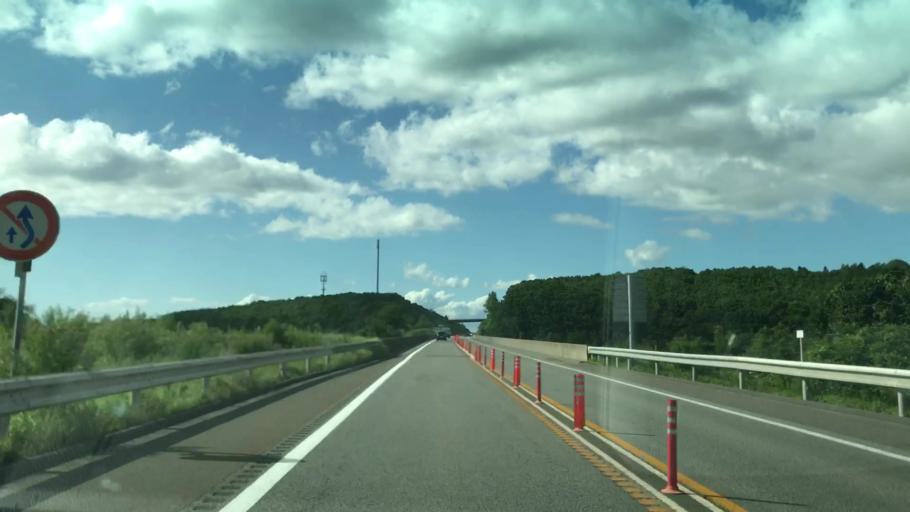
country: JP
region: Hokkaido
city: Muroran
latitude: 42.3927
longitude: 140.9578
